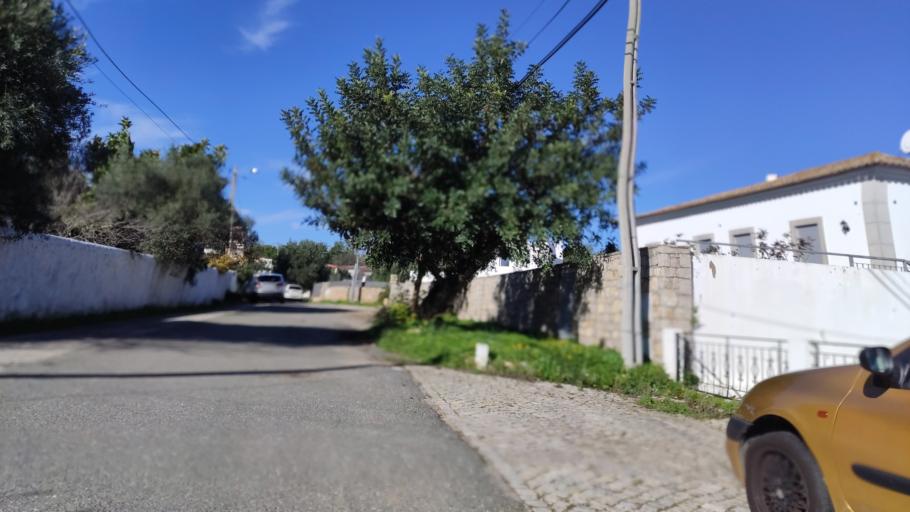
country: PT
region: Faro
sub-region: Sao Bras de Alportel
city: Sao Bras de Alportel
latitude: 37.1482
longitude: -7.8785
